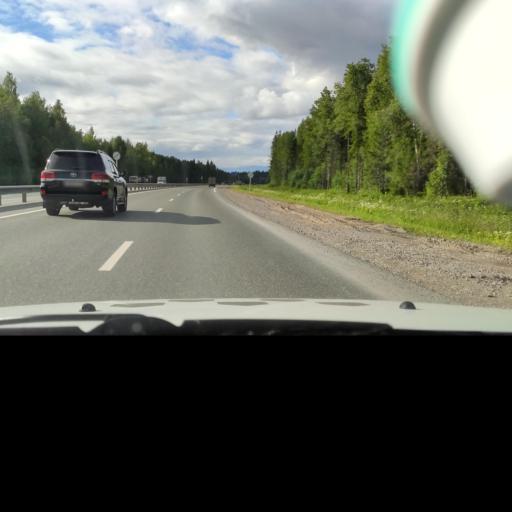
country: RU
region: Perm
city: Polazna
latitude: 58.2470
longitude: 56.4130
